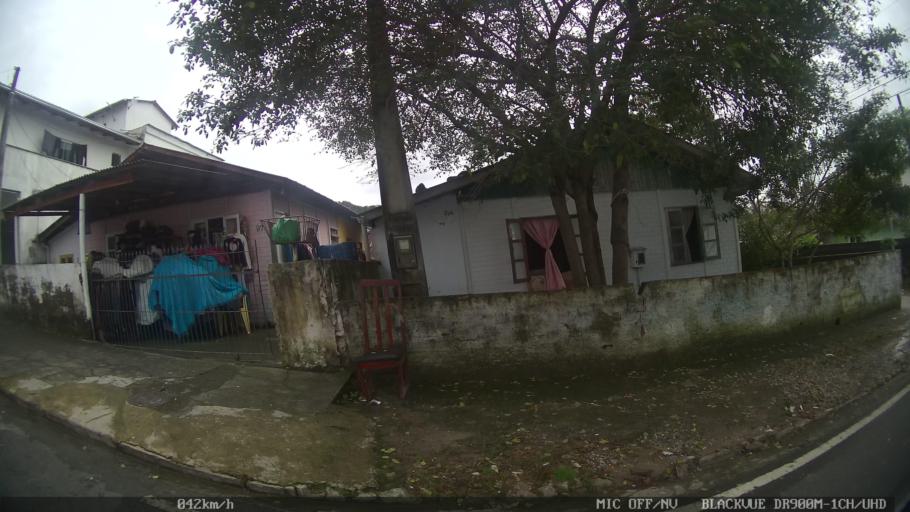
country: BR
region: Santa Catarina
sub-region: Biguacu
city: Biguacu
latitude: -27.5428
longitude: -48.6476
